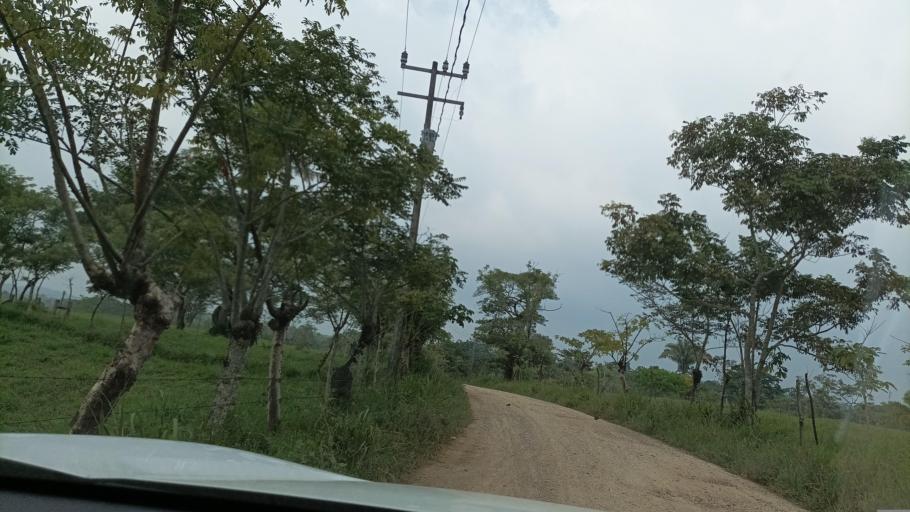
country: MX
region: Tabasco
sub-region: Huimanguillo
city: Francisco Rueda
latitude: 17.5963
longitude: -94.1971
